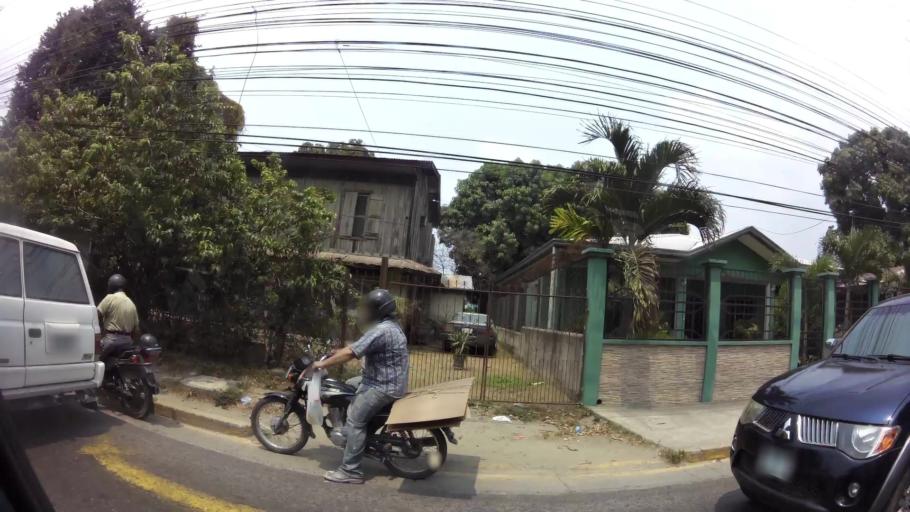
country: HN
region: Yoro
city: El Progreso
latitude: 15.3933
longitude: -87.8075
